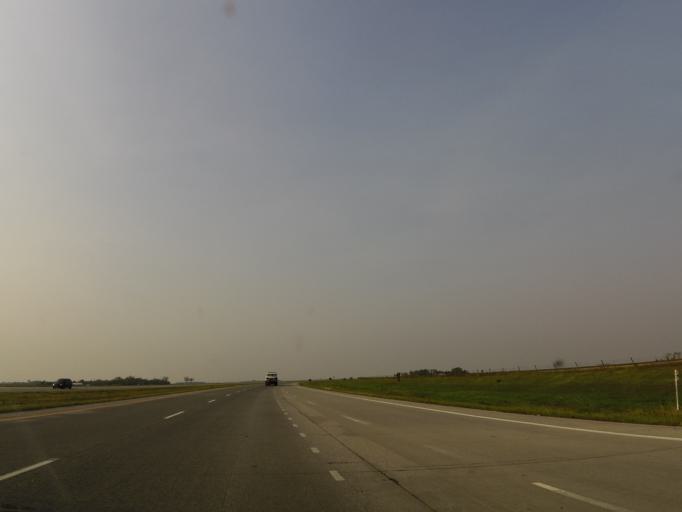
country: US
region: North Dakota
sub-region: Cass County
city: West Fargo
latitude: 47.0530
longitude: -96.9415
